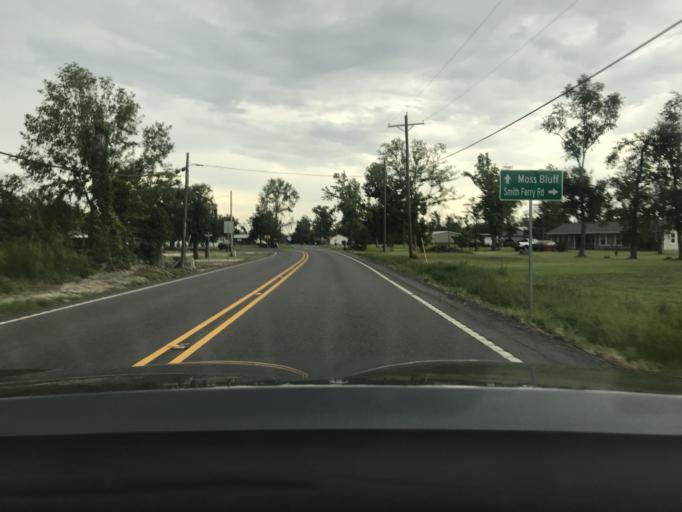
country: US
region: Louisiana
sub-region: Calcasieu Parish
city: Westlake
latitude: 30.2707
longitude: -93.2418
